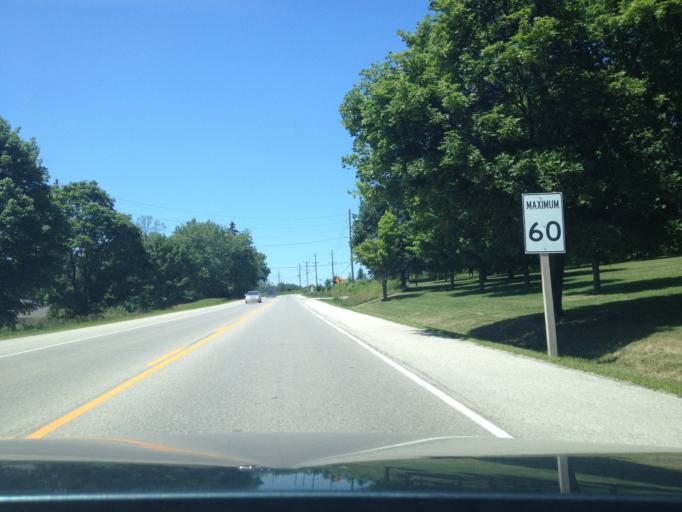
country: CA
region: Ontario
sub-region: Wellington County
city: Guelph
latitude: 43.6918
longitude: -80.4000
